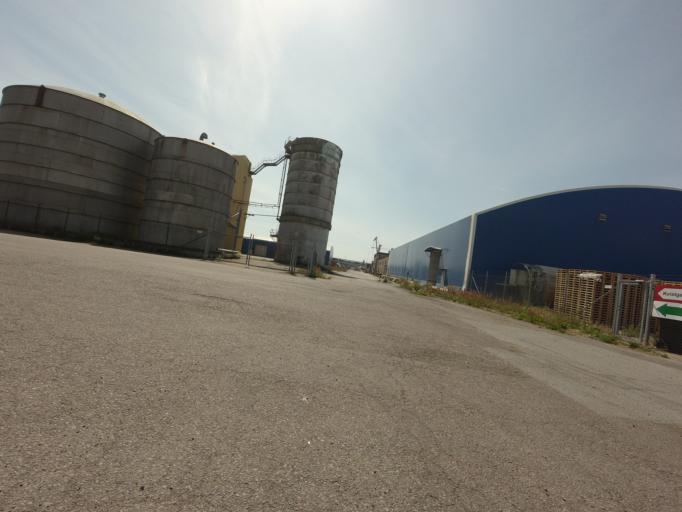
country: SE
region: Skane
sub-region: Landskrona
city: Landskrona
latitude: 55.8621
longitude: 12.8305
